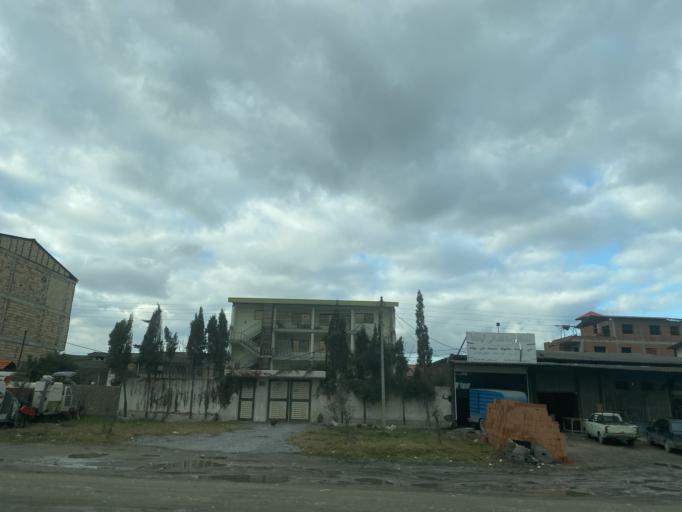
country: IR
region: Mazandaran
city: Amol
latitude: 36.4361
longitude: 52.3715
